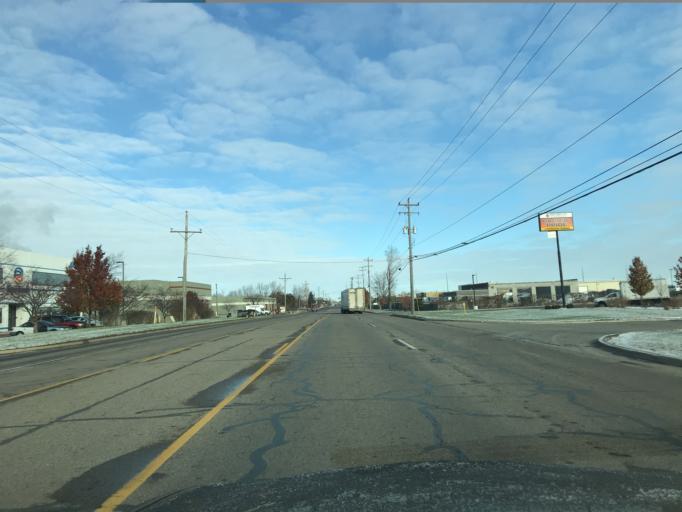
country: US
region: Michigan
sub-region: Eaton County
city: Dimondale
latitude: 42.6873
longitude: -84.6424
